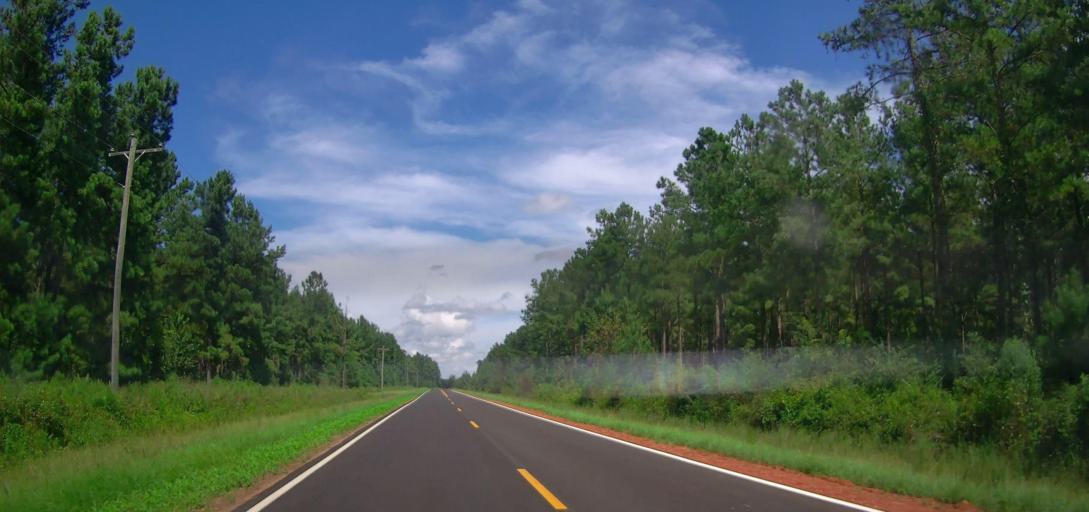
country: US
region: Georgia
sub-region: Macon County
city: Marshallville
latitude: 32.4699
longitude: -83.8977
